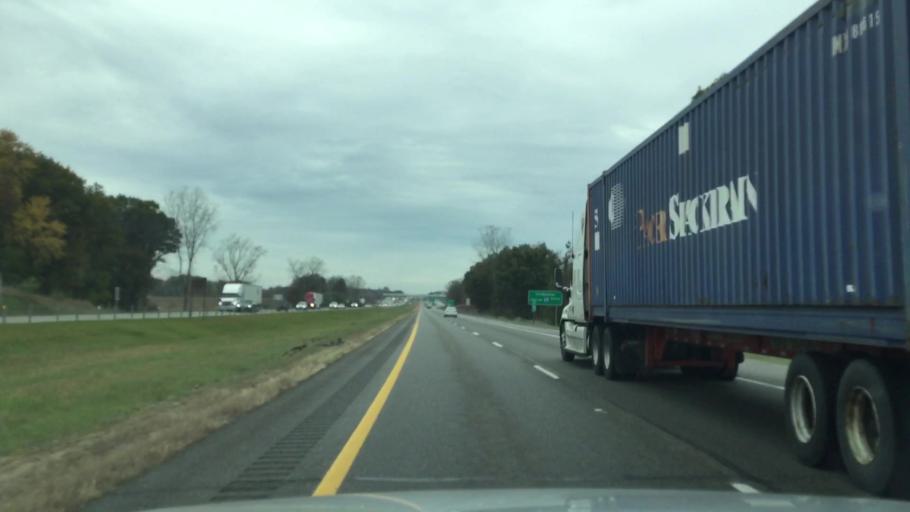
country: US
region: Michigan
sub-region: Calhoun County
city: Marshall
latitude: 42.2973
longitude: -84.9765
